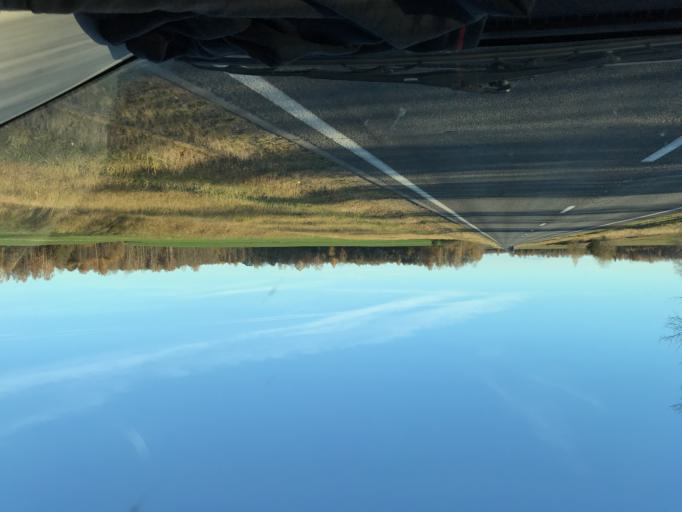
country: BY
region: Vitebsk
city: Haradok
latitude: 55.4104
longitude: 30.1119
